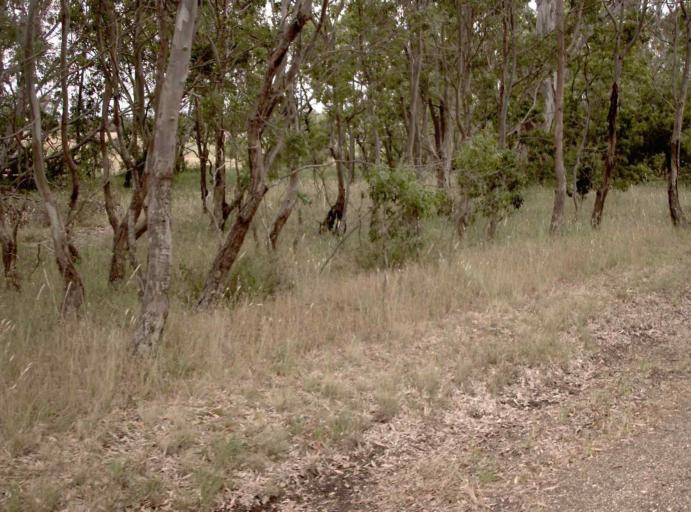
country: AU
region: Victoria
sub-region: Wellington
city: Sale
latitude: -37.9597
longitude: 147.1055
